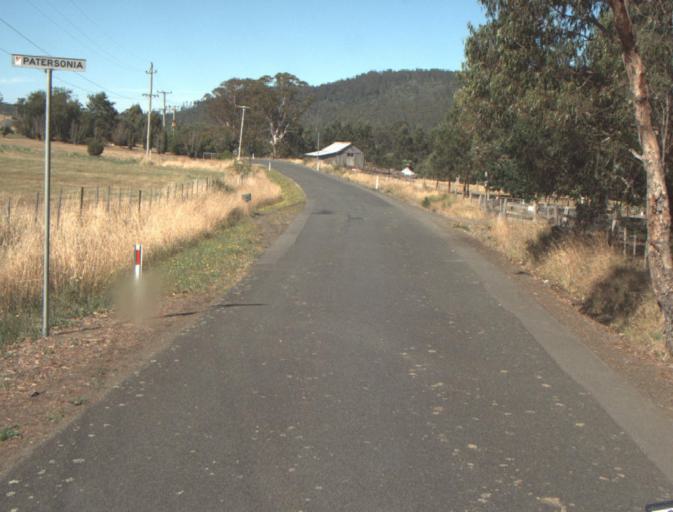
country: AU
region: Tasmania
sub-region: Launceston
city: Newstead
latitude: -41.3384
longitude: 147.3037
